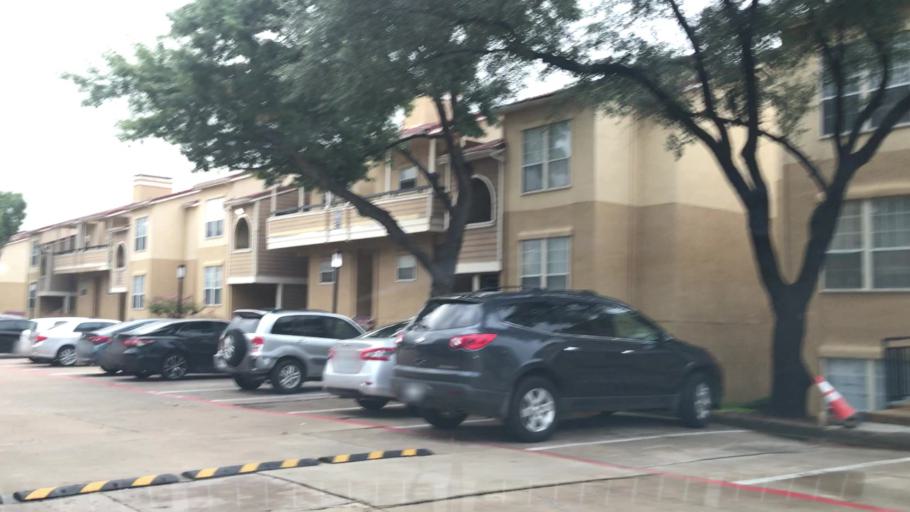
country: US
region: Texas
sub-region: Dallas County
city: Irving
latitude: 32.8831
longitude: -96.9733
